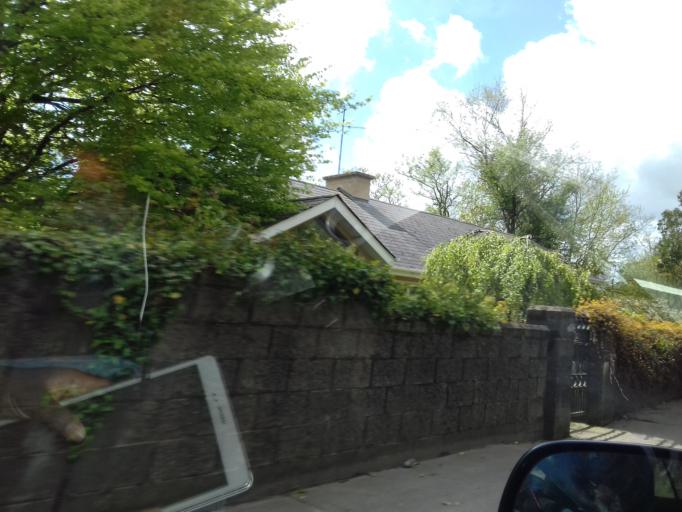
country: IE
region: Leinster
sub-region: Loch Garman
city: Loch Garman
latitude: 52.3274
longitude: -6.4763
